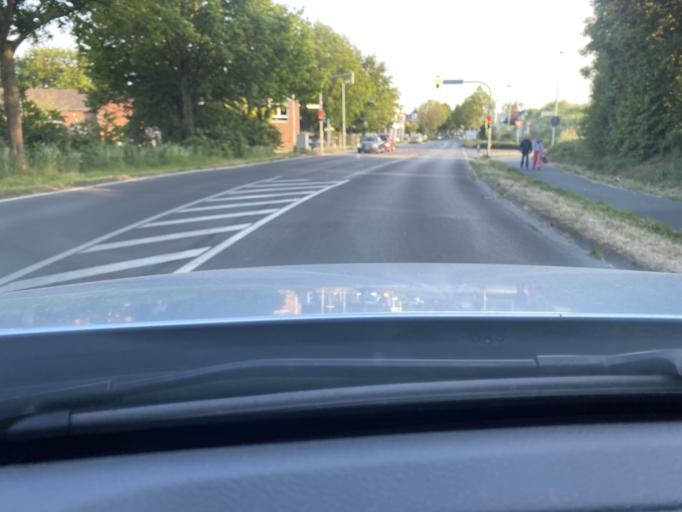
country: DE
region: North Rhine-Westphalia
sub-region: Regierungsbezirk Dusseldorf
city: Grevenbroich
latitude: 51.0984
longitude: 6.5834
